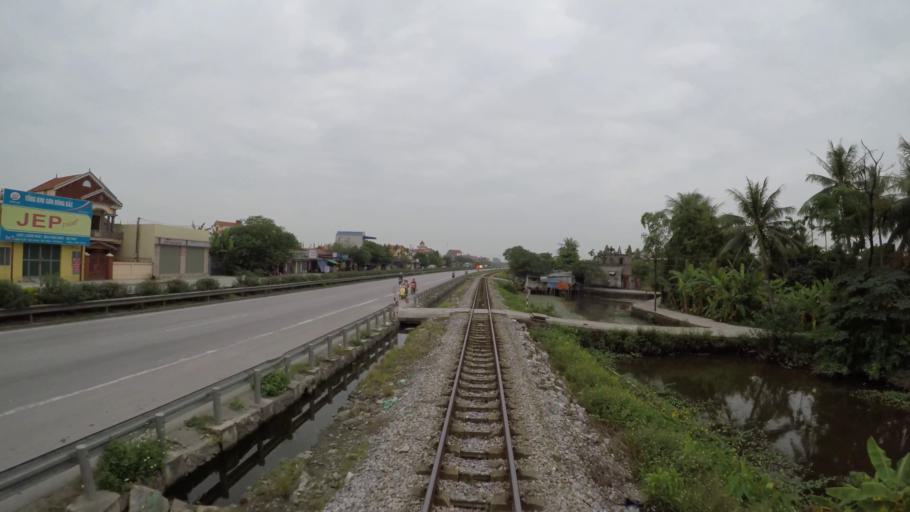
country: VN
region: Hai Duong
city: Phu Thai
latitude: 20.9594
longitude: 106.5227
